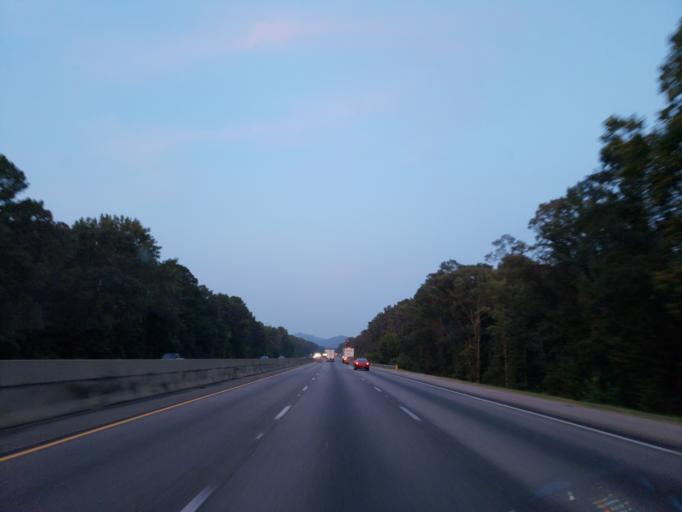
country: US
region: Alabama
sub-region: Saint Clair County
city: Moody
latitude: 33.5709
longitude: -86.4961
